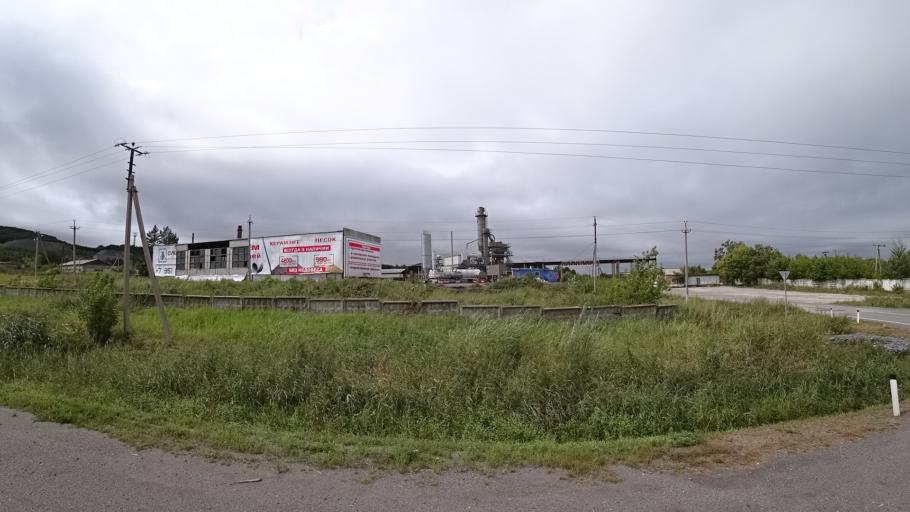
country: RU
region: Primorskiy
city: Monastyrishche
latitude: 44.1693
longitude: 132.4410
